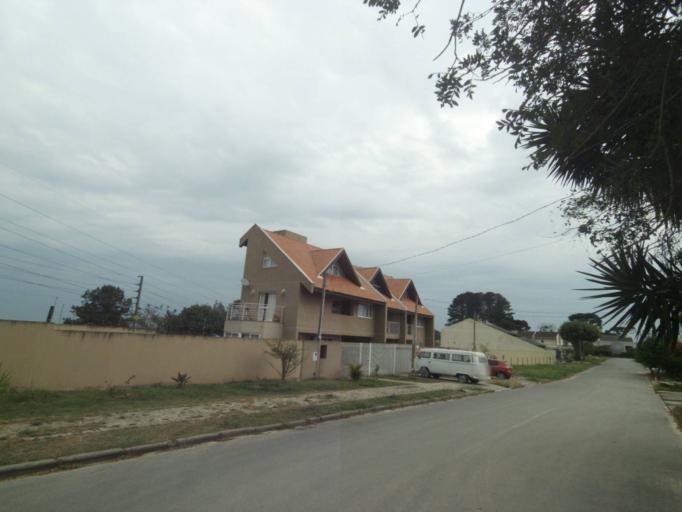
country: BR
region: Parana
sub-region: Pinhais
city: Pinhais
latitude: -25.4845
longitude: -49.2156
